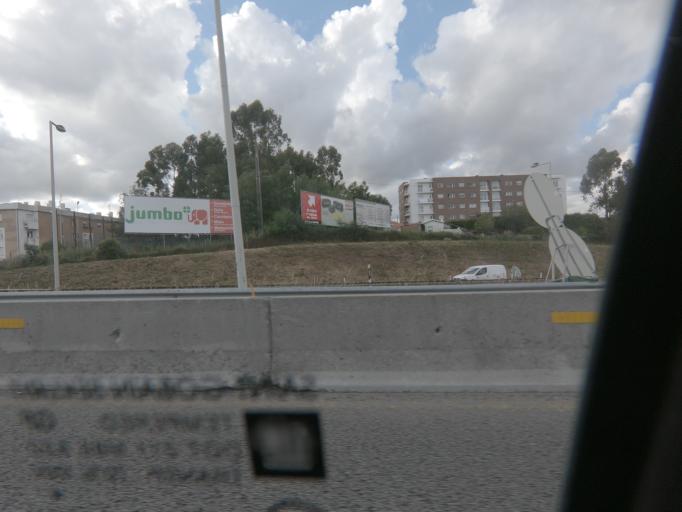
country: PT
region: Porto
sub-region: Gondomar
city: Baguim do Monte
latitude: 41.2011
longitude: -8.5546
